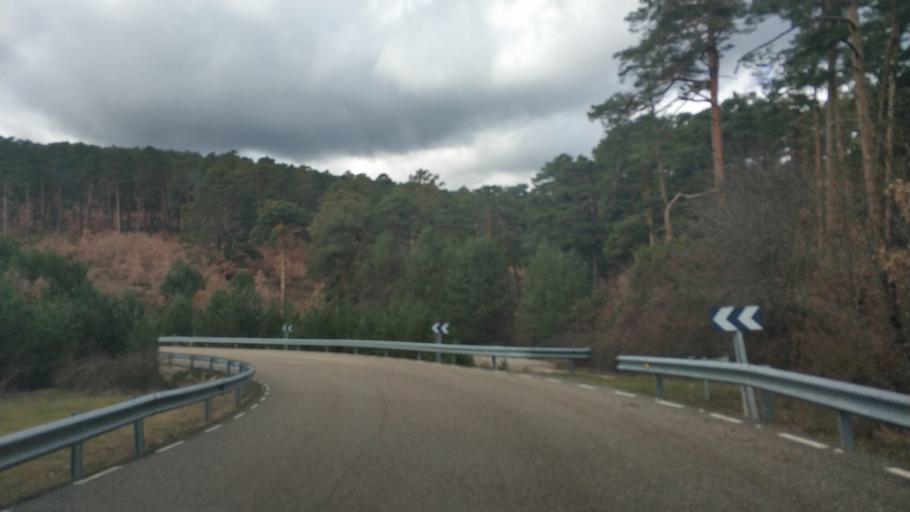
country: ES
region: Castille and Leon
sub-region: Provincia de Burgos
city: Quintanar de la Sierra
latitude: 41.9951
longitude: -3.0226
